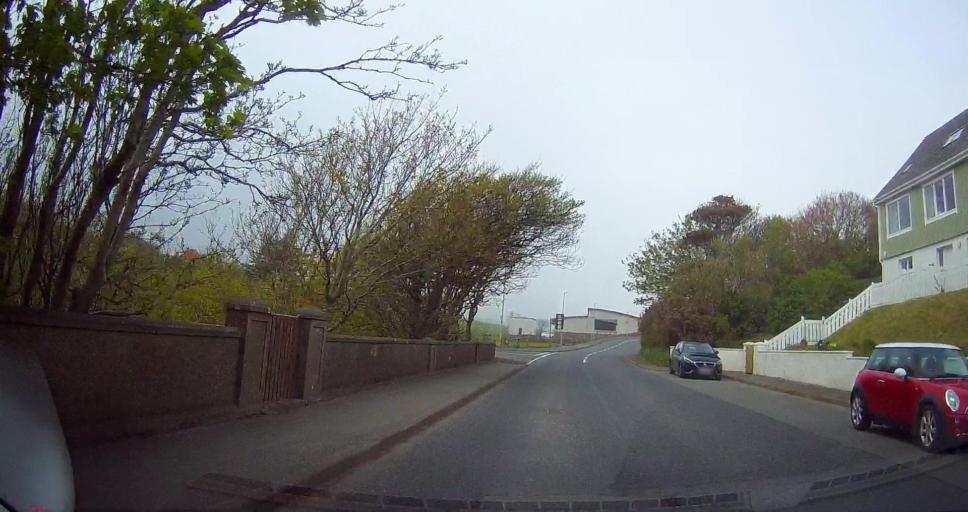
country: GB
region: Scotland
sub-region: Shetland Islands
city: Lerwick
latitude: 60.1383
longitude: -1.2744
